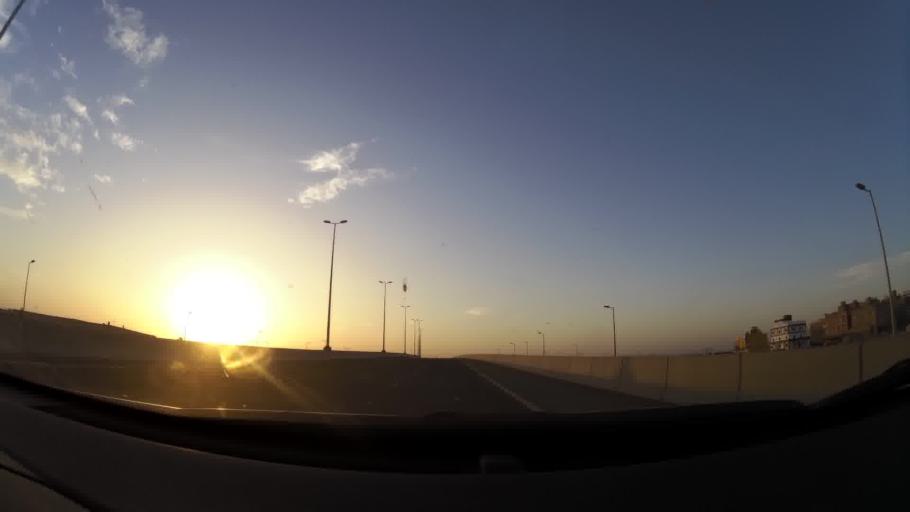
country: KW
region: Al Asimah
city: Ar Rabiyah
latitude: 29.3206
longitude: 47.8064
